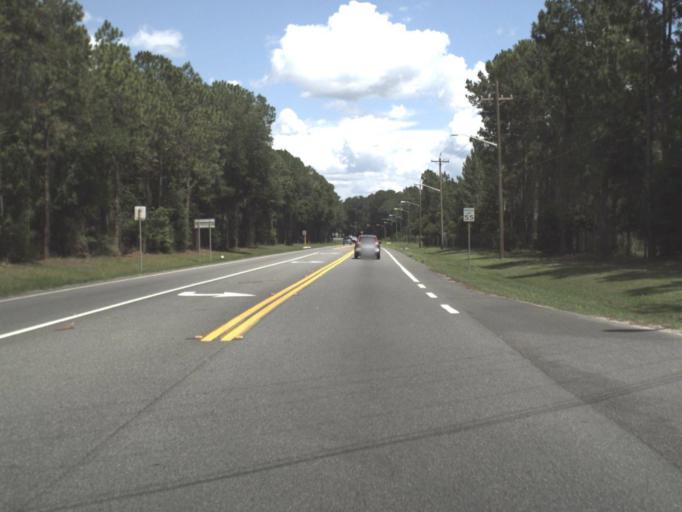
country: US
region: Florida
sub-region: Alachua County
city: Gainesville
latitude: 29.6767
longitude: -82.2733
